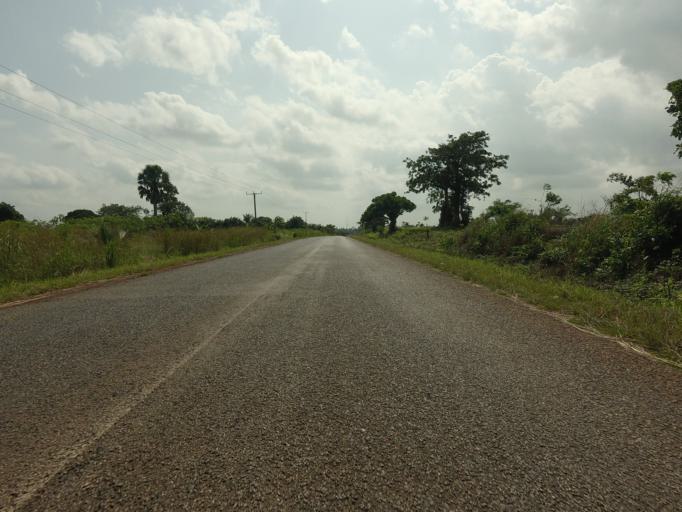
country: GH
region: Volta
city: Ho
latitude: 6.4087
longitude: 0.7676
